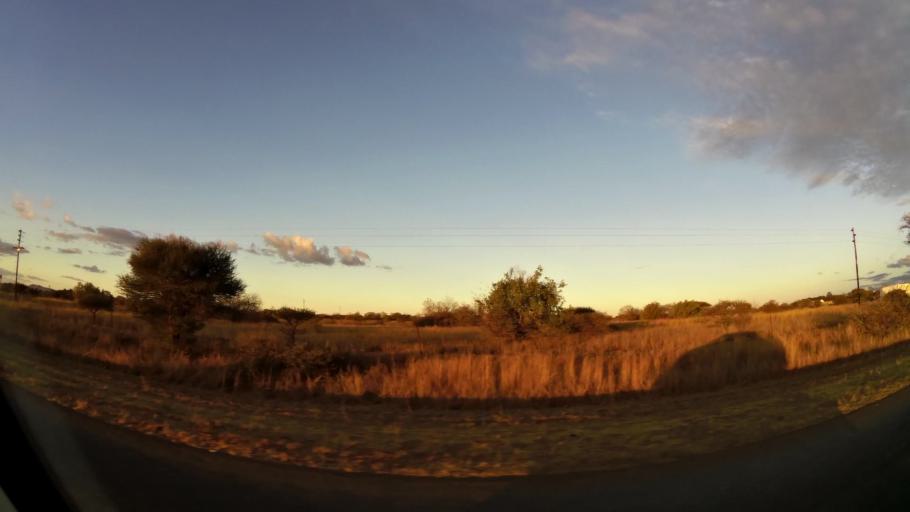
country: ZA
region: Limpopo
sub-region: Capricorn District Municipality
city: Polokwane
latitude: -23.8110
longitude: 29.4800
